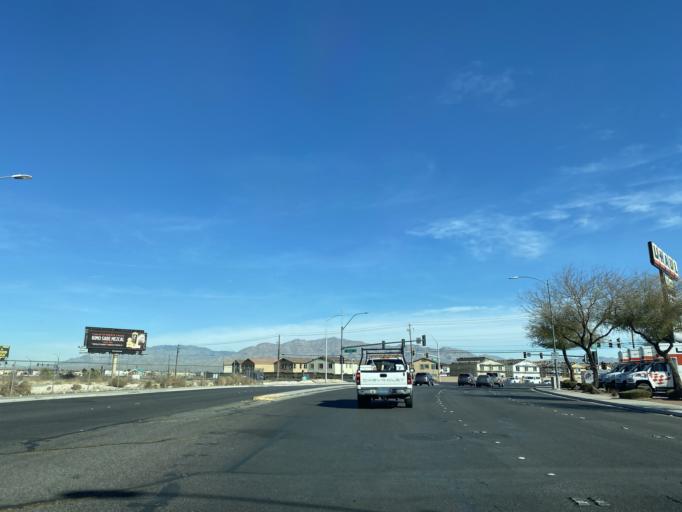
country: US
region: Nevada
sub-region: Clark County
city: Las Vegas
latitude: 36.2303
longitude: -115.2254
